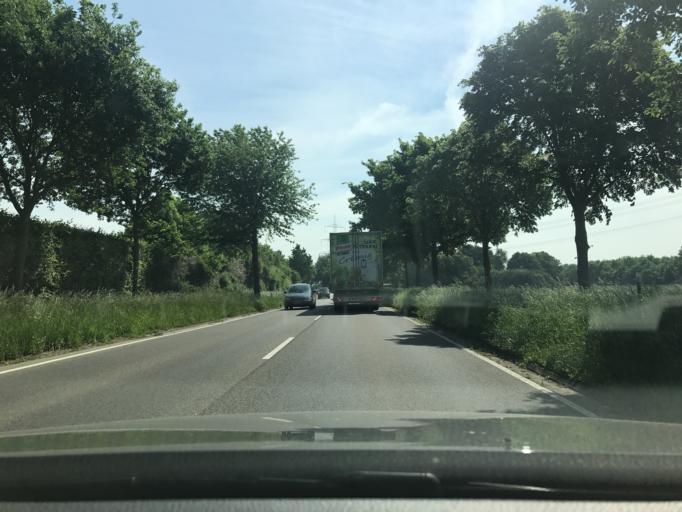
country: DE
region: North Rhine-Westphalia
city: Tonisvorst
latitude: 51.3120
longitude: 6.4855
